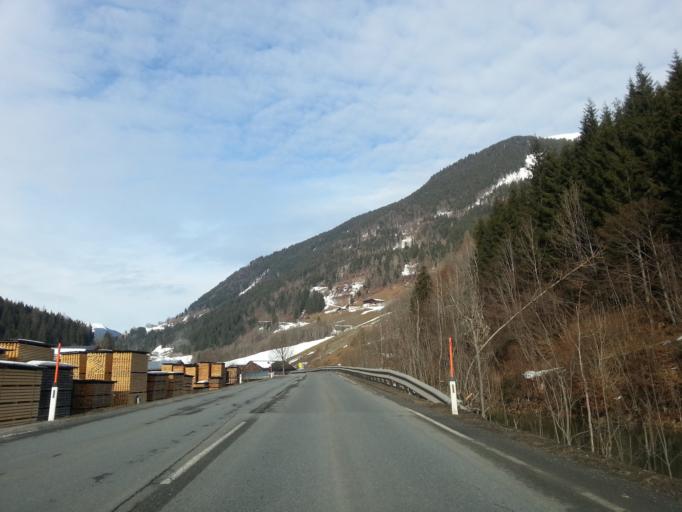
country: AT
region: Salzburg
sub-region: Politischer Bezirk Zell am See
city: Maishofen
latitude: 47.3644
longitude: 12.7842
